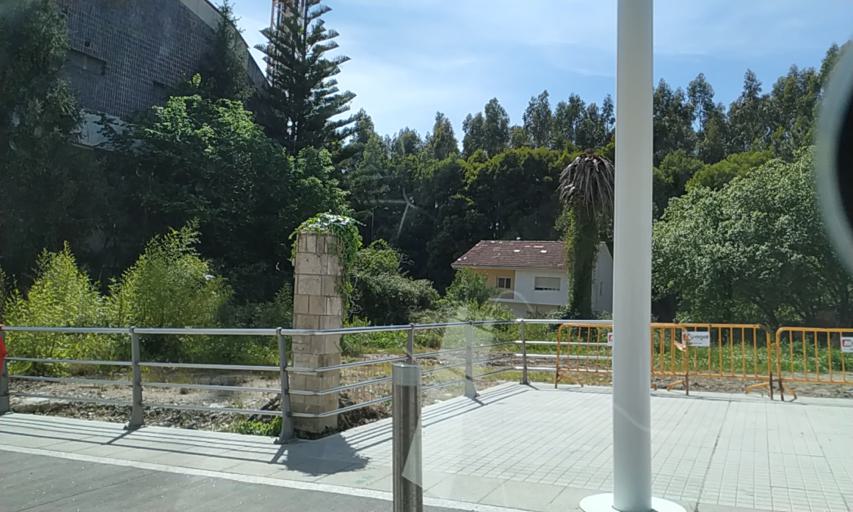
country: ES
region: Galicia
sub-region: Provincia de Pontevedra
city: Sanxenxo
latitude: 42.4041
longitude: -8.8127
